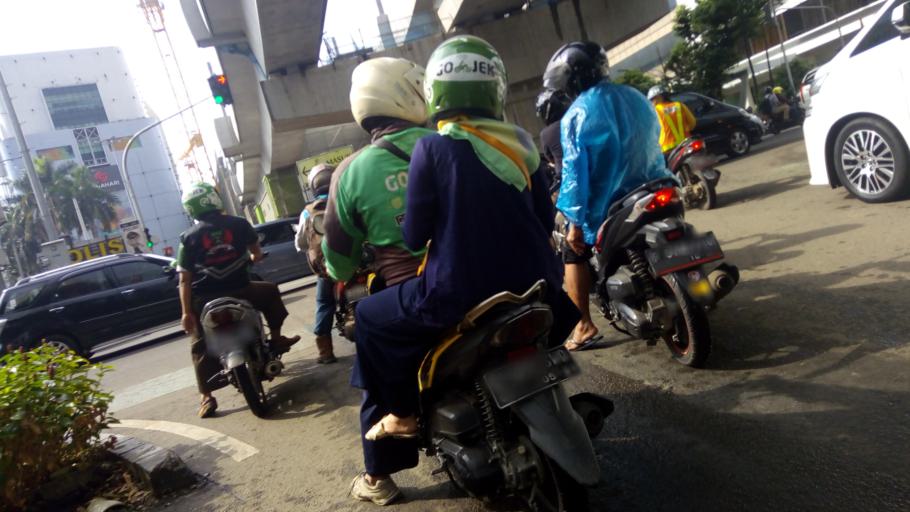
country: ID
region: Jakarta Raya
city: Jakarta
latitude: -6.2463
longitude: 106.7979
